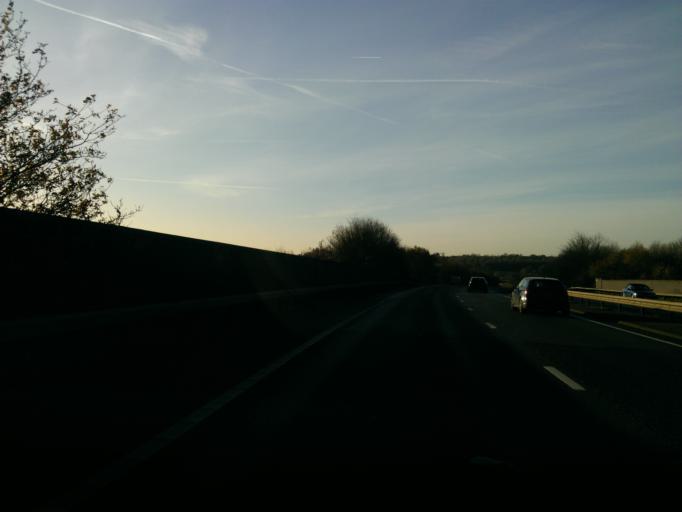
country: GB
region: England
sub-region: Essex
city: West Bergholt
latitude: 51.9021
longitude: 0.8657
